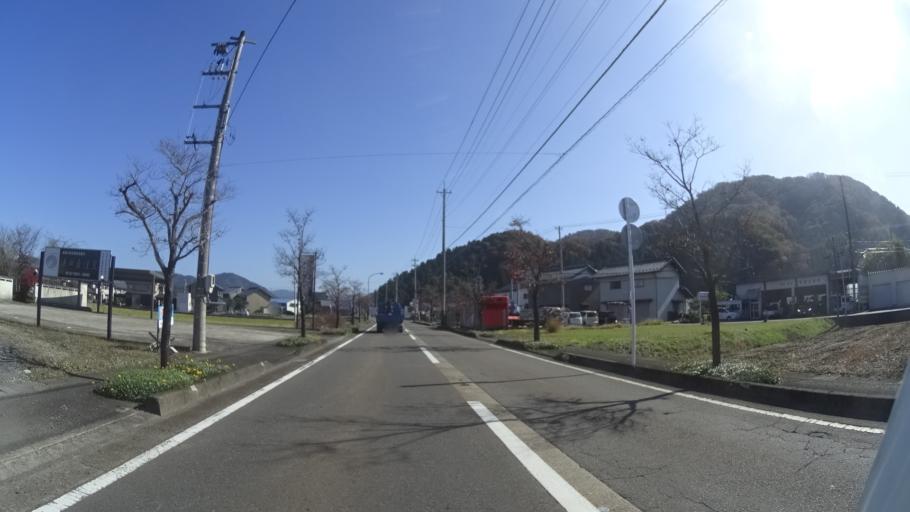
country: JP
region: Fukui
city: Sabae
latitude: 35.9494
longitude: 136.2098
